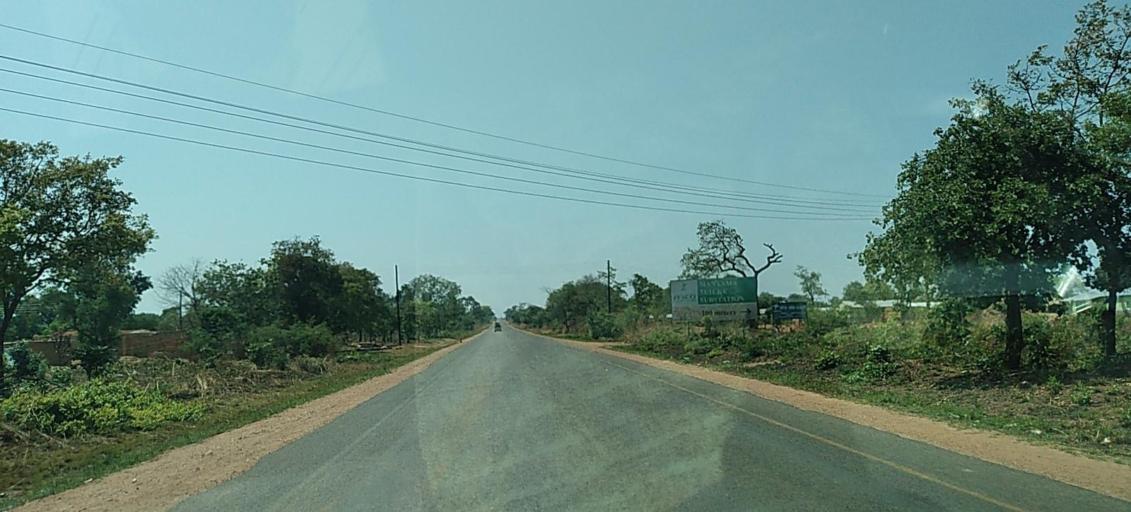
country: ZM
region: North-Western
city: Solwezi
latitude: -12.3012
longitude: 25.8322
